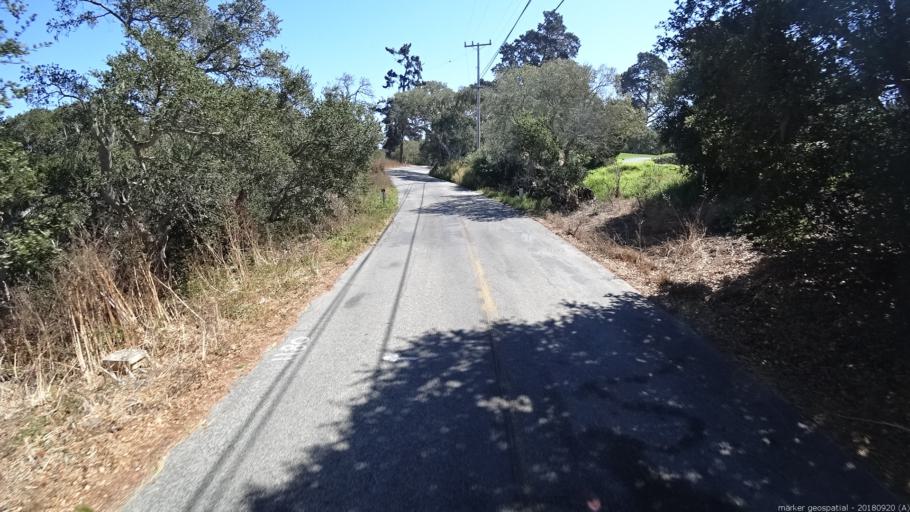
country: US
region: California
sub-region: Monterey County
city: Monterey
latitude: 36.5869
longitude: -121.8704
